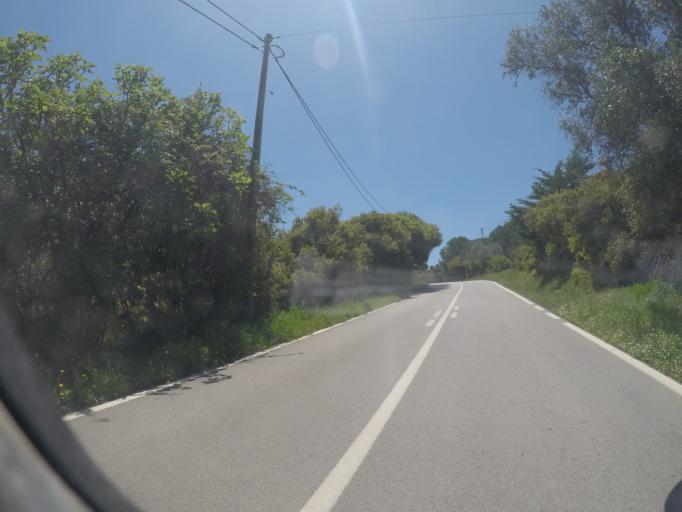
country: PT
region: Setubal
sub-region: Sesimbra
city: Sesimbra
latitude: 38.4740
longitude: -9.0295
